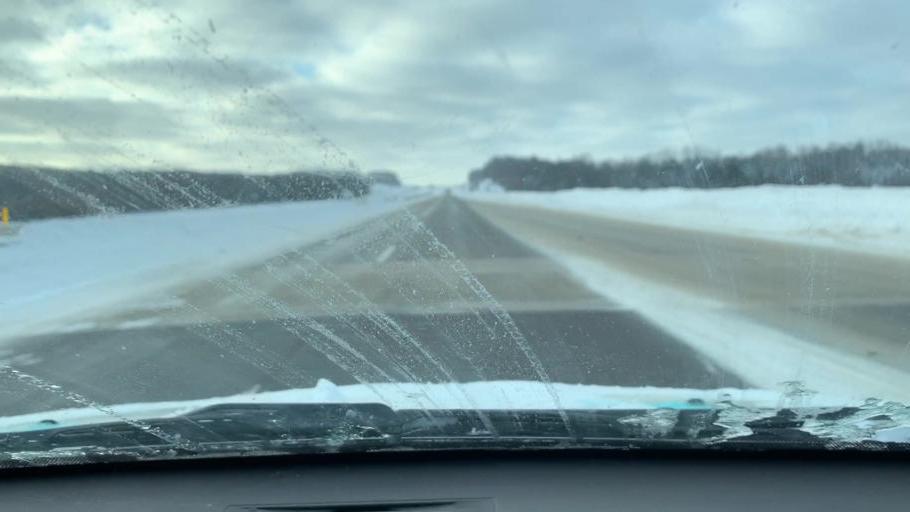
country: US
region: Michigan
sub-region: Wexford County
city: Manton
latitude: 44.4055
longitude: -85.3815
